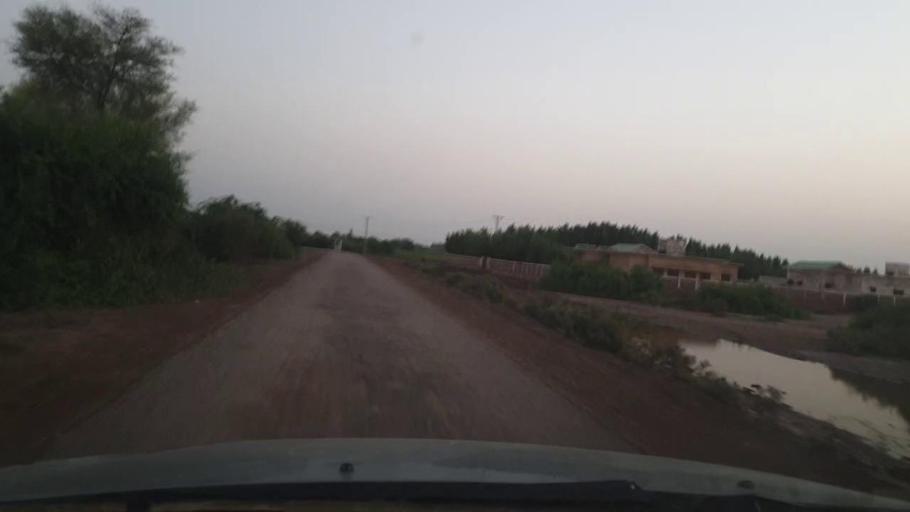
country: PK
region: Sindh
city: Digri
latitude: 25.1218
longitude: 69.0056
